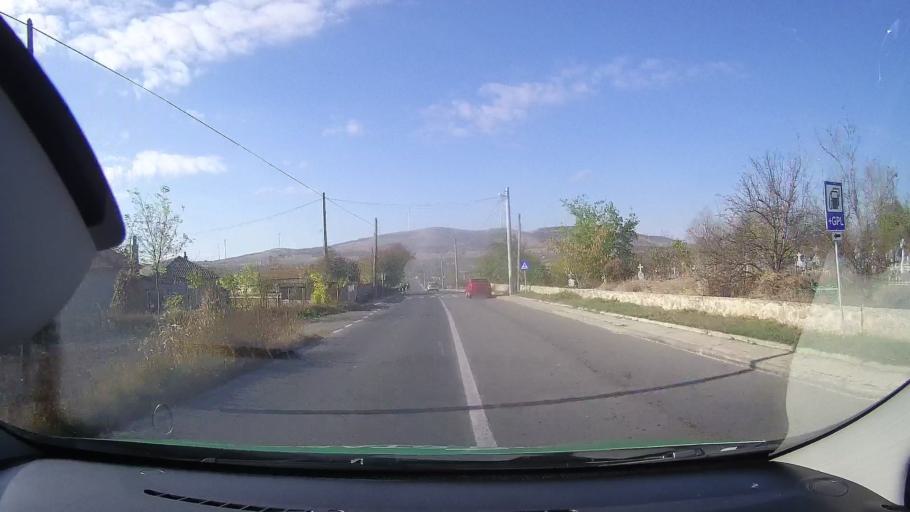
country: RO
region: Tulcea
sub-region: Comuna Valea Nucarilor
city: Agighiol
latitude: 45.0343
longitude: 28.8858
